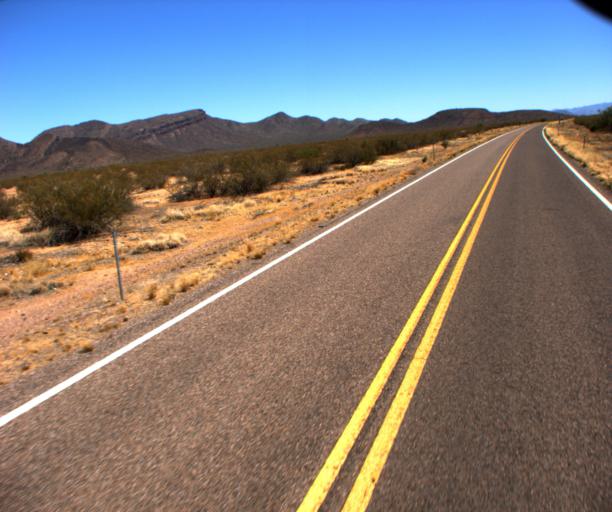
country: US
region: Arizona
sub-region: Yavapai County
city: Congress
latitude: 33.9908
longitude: -113.1329
